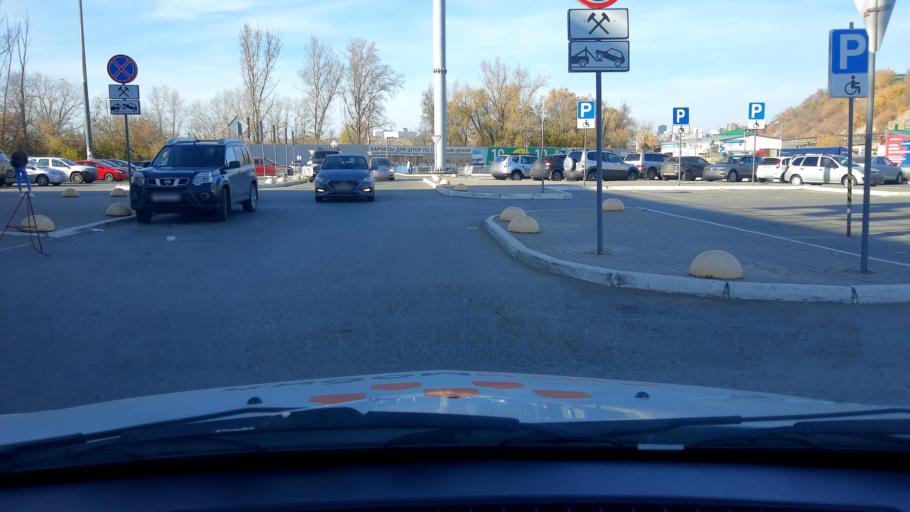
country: RU
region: Bashkortostan
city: Ufa
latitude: 54.6966
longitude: 55.9719
